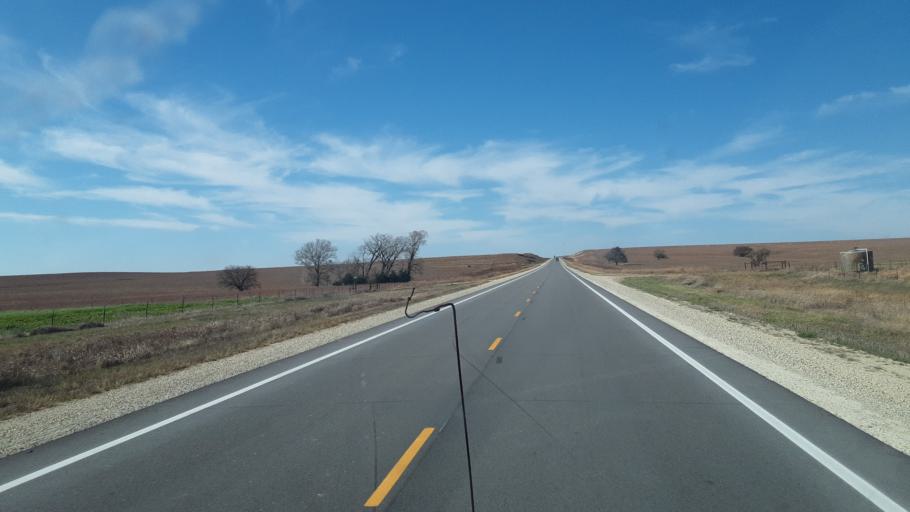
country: US
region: Kansas
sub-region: Chase County
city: Cottonwood Falls
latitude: 38.3627
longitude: -96.6799
